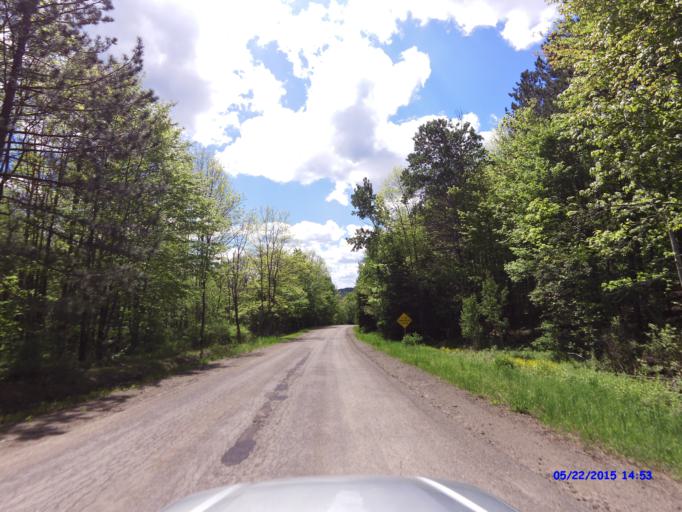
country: US
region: New York
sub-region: Cattaraugus County
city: Franklinville
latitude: 42.3812
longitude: -78.5825
